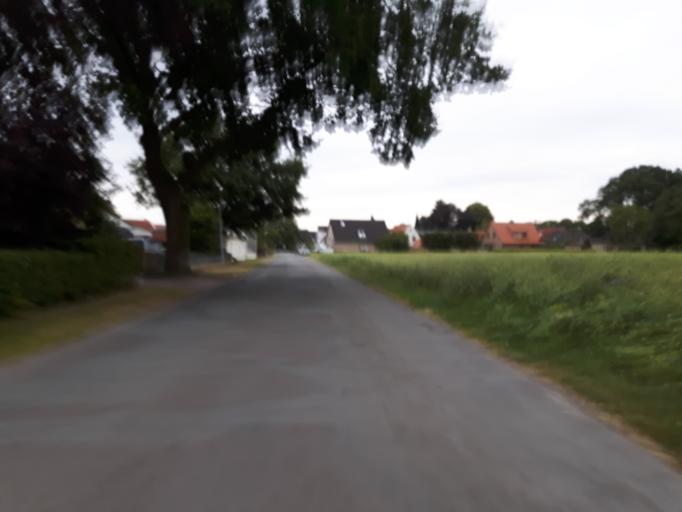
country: DE
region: Lower Saxony
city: Stuhr
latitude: 53.0376
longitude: 8.7104
